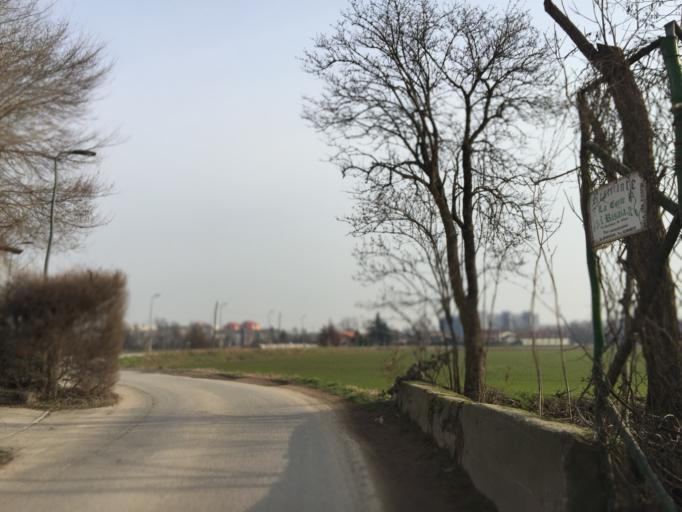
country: IT
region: Lombardy
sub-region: Citta metropolitana di Milano
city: Romano Banco
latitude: 45.4275
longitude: 9.1398
